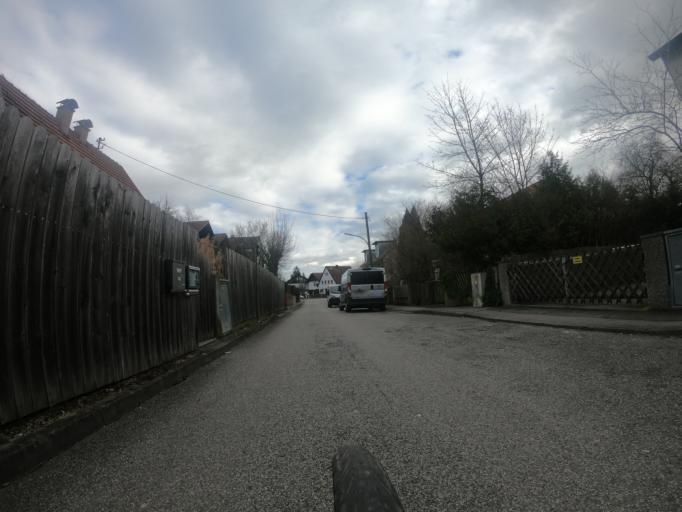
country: DE
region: Bavaria
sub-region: Upper Bavaria
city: Schongeising
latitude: 48.1605
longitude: 11.2276
